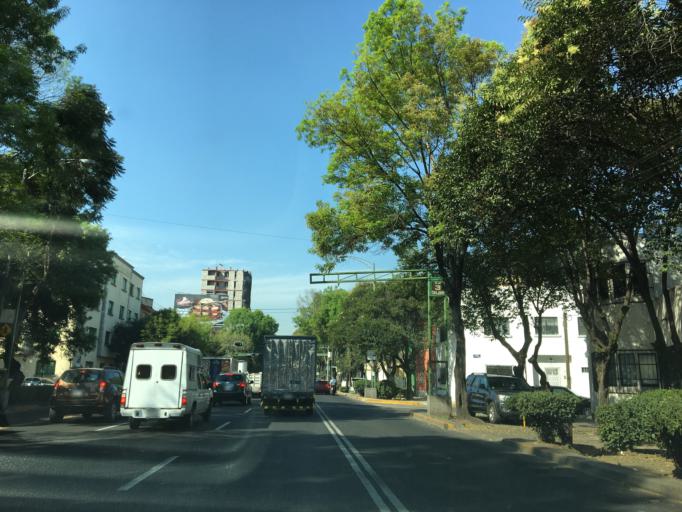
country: MX
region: Mexico City
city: Benito Juarez
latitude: 19.4059
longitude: -99.1741
